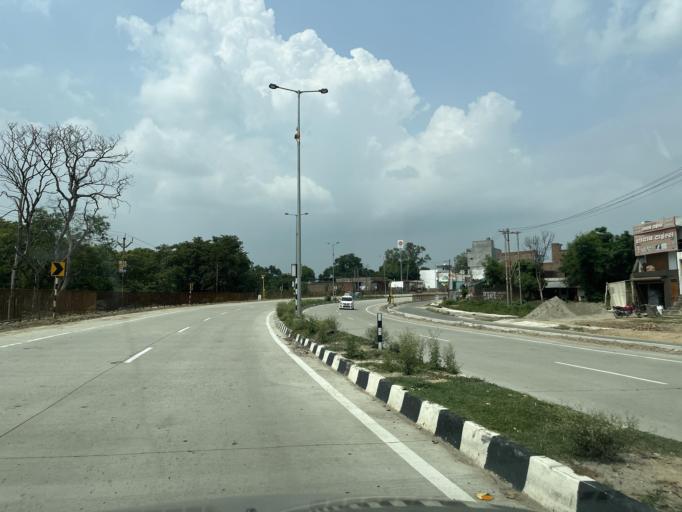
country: IN
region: Uttar Pradesh
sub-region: Bijnor
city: Sherkot
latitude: 29.3320
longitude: 78.5677
